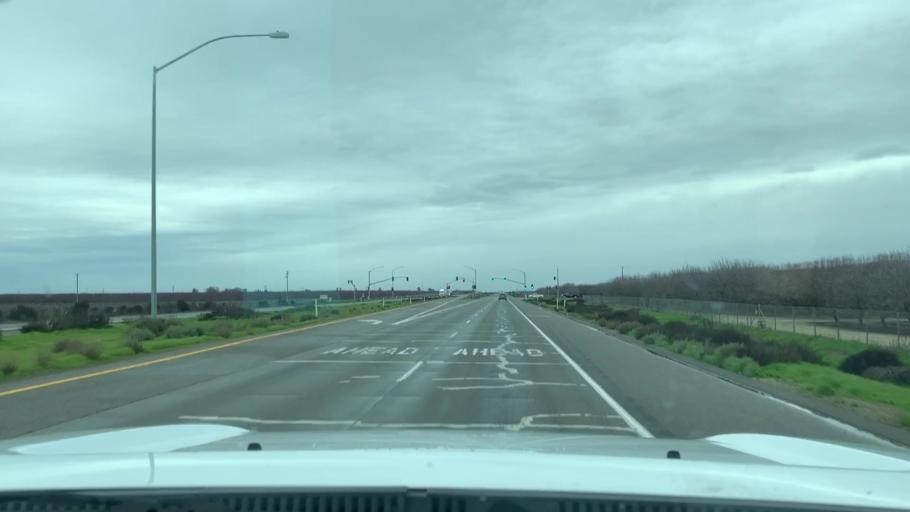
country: US
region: California
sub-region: Fresno County
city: Caruthers
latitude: 36.5160
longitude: -119.7861
